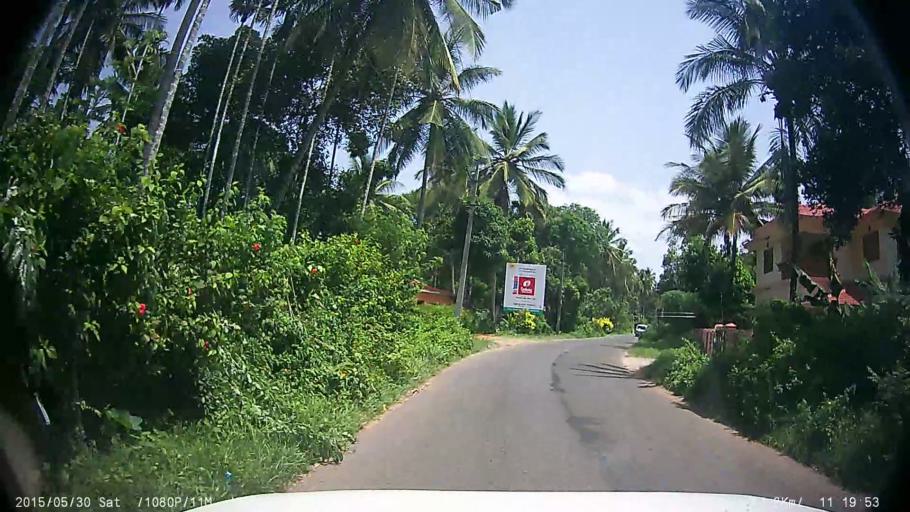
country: IN
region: Kerala
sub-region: Wayanad
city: Panamaram
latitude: 11.7916
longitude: 76.0423
